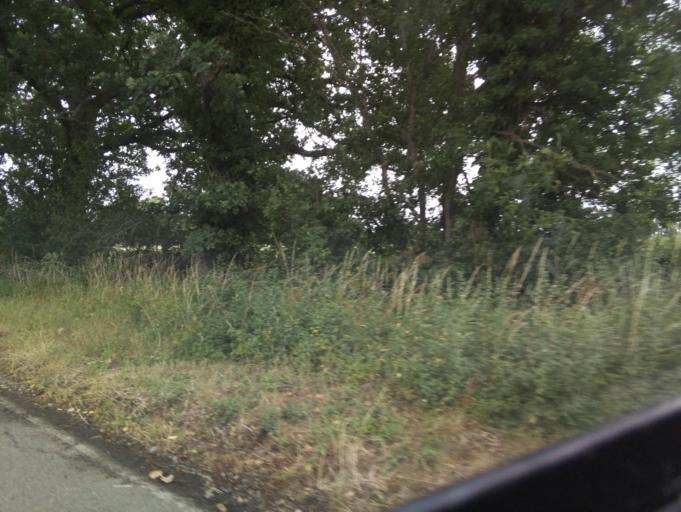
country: GB
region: England
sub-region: Derbyshire
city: Findern
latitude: 52.8829
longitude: -1.5293
